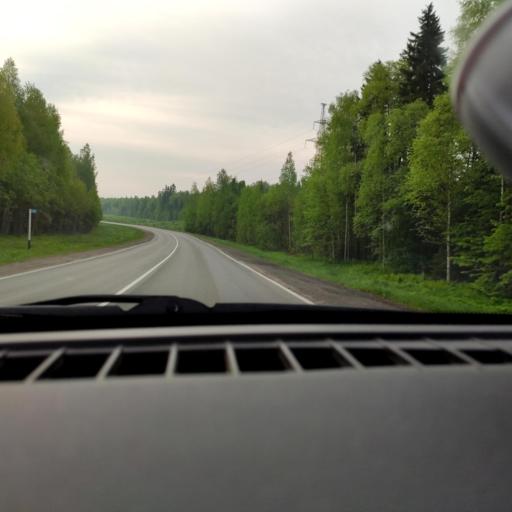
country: RU
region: Perm
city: Perm
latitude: 58.1394
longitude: 56.2714
